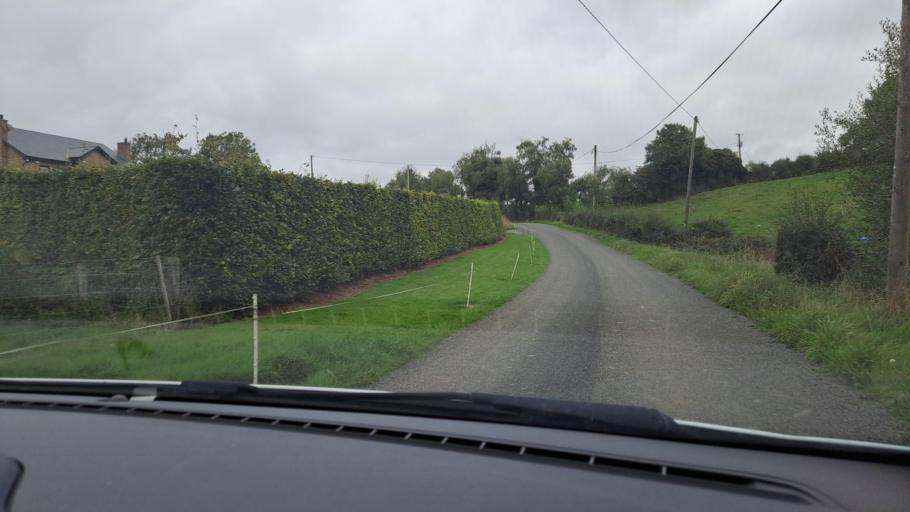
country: IE
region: Ulster
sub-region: County Monaghan
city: Carrickmacross
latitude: 54.0352
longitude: -6.8111
